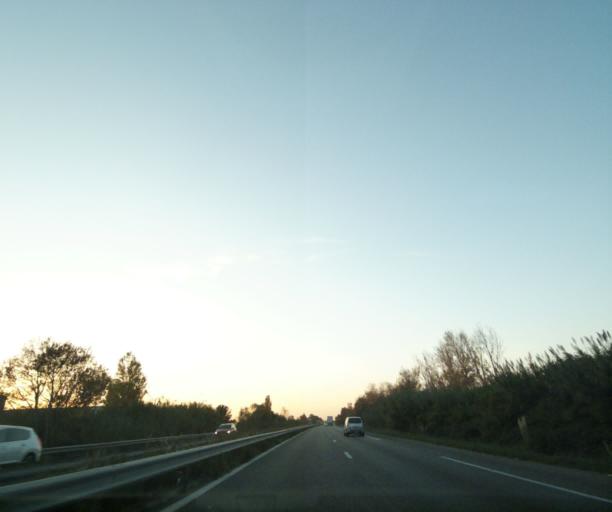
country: FR
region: Provence-Alpes-Cote d'Azur
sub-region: Departement des Bouches-du-Rhone
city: Saint-Martin-de-Crau
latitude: 43.6304
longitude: 4.7977
